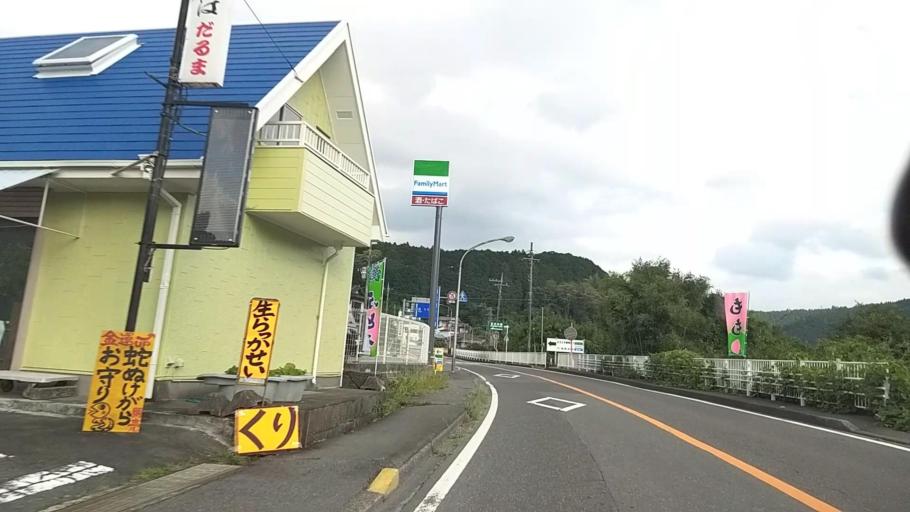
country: JP
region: Shizuoka
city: Fujinomiya
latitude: 35.1990
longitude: 138.5605
